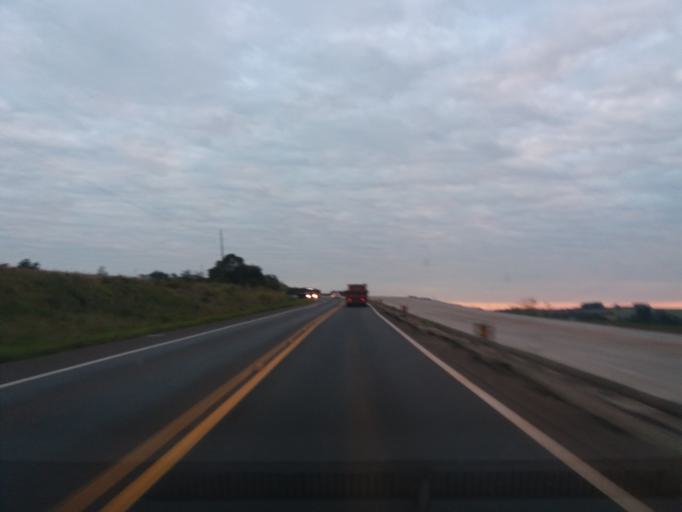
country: BR
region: Parana
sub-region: Realeza
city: Realeza
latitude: -25.3866
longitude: -53.5768
